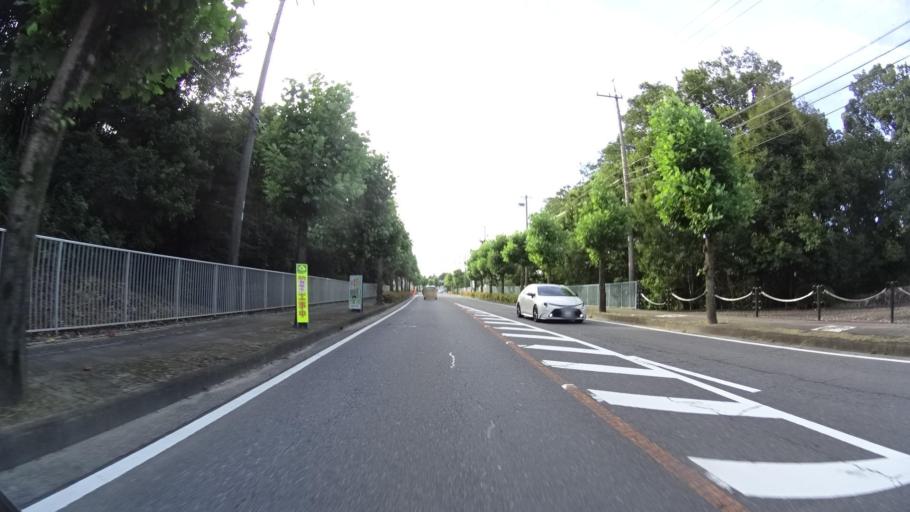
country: JP
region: Mie
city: Kawage
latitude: 34.8501
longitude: 136.5360
